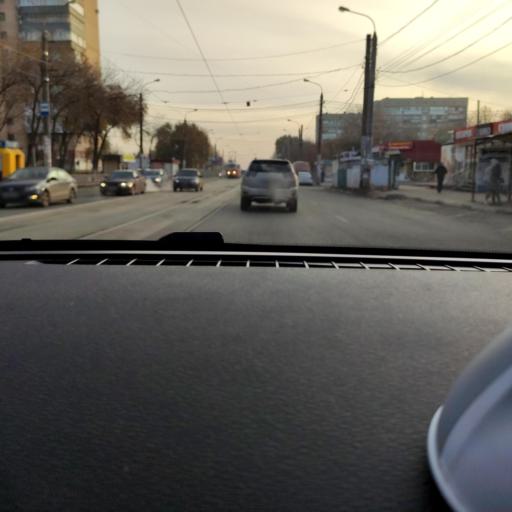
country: RU
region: Samara
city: Samara
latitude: 53.1918
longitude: 50.1973
